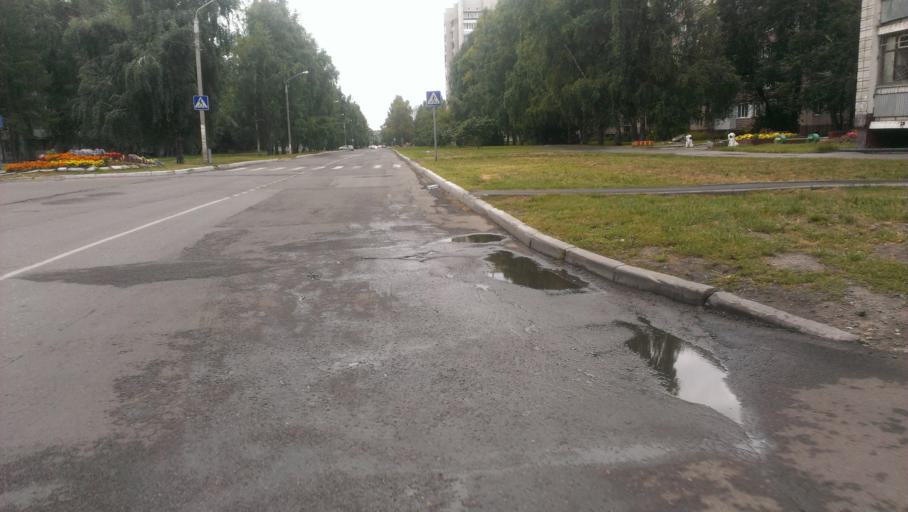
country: RU
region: Altai Krai
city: Novosilikatnyy
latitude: 53.3715
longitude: 83.6696
